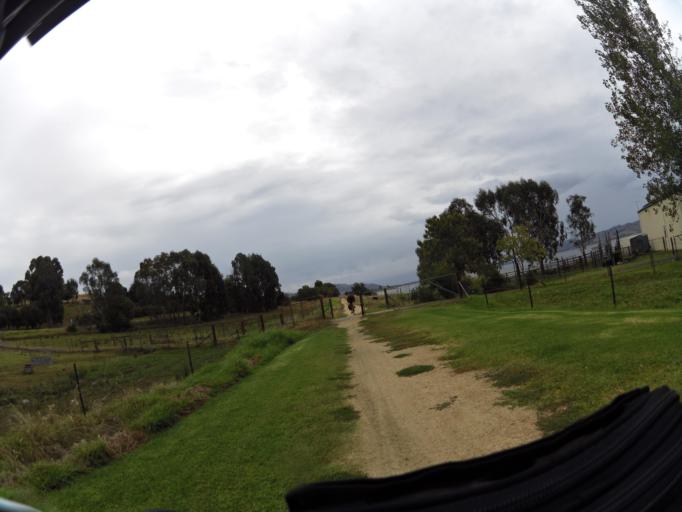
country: AU
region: New South Wales
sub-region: Albury Municipality
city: East Albury
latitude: -36.2245
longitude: 147.0747
